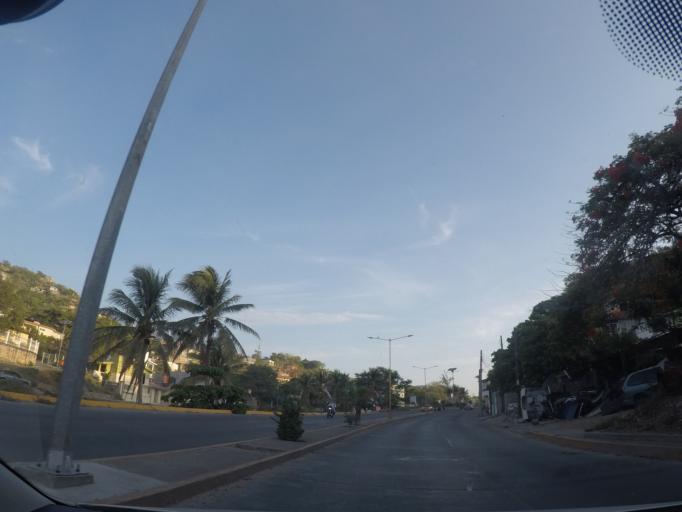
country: MX
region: Oaxaca
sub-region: Salina Cruz
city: Salina Cruz
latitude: 16.1883
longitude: -95.2015
